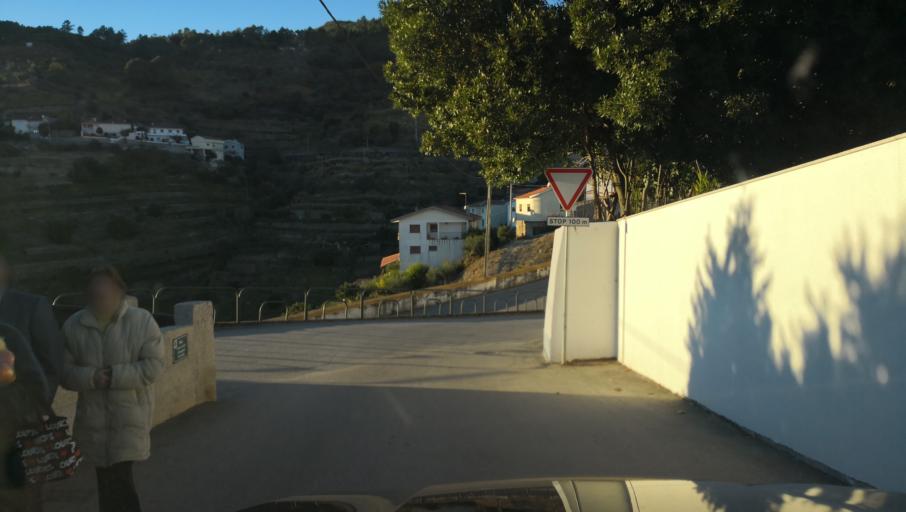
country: PT
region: Vila Real
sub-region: Santa Marta de Penaguiao
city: Santa Marta de Penaguiao
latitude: 41.2508
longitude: -7.7708
